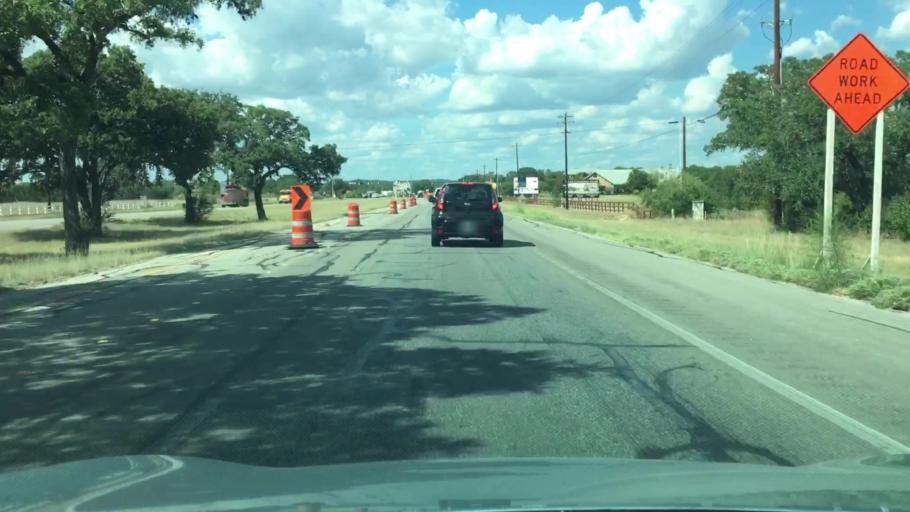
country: US
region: Texas
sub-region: Comal County
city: Bulverde
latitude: 29.8467
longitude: -98.4089
